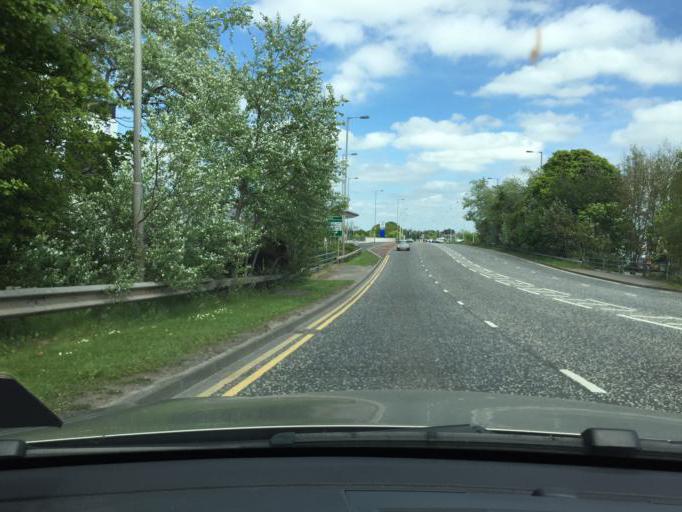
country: GB
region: Northern Ireland
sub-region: Armagh District
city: Portadown
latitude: 54.4235
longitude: -6.4473
